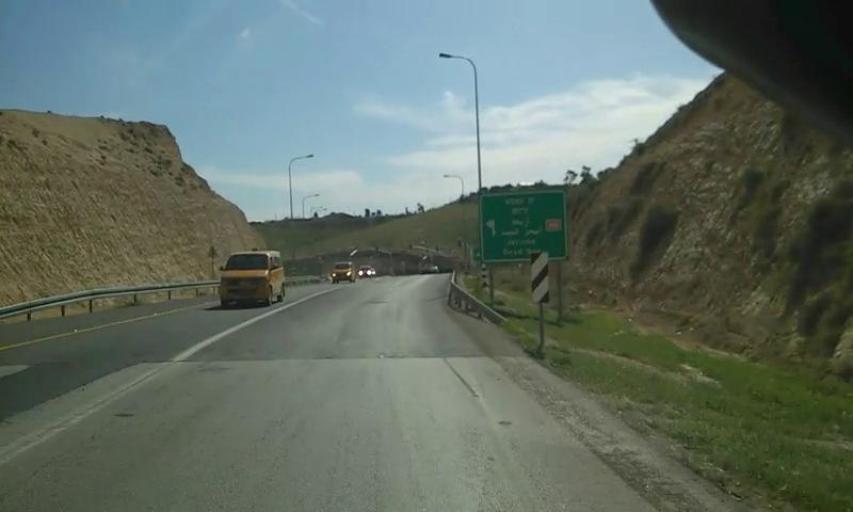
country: PS
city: Az Za`ayyim
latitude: 31.8066
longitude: 35.3249
